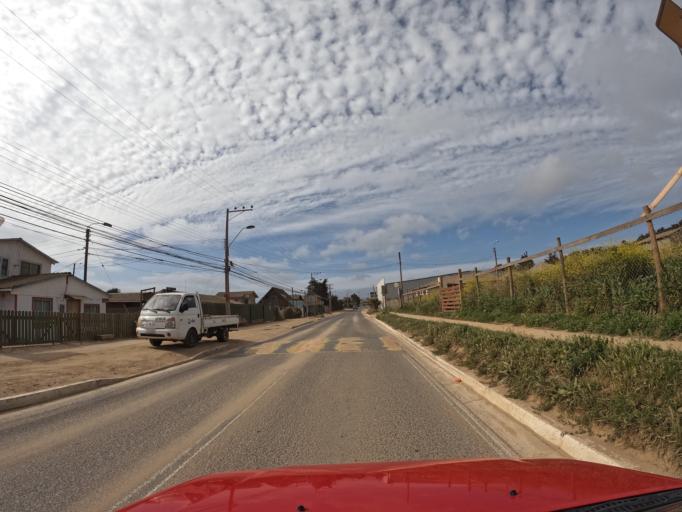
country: CL
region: O'Higgins
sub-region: Provincia de Colchagua
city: Santa Cruz
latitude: -34.4012
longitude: -72.0237
